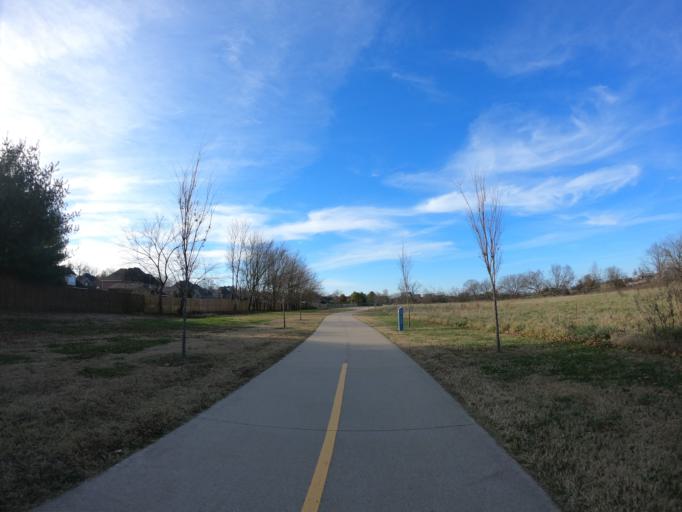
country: US
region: Arkansas
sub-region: Benton County
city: Lowell
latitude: 36.2920
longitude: -94.1727
